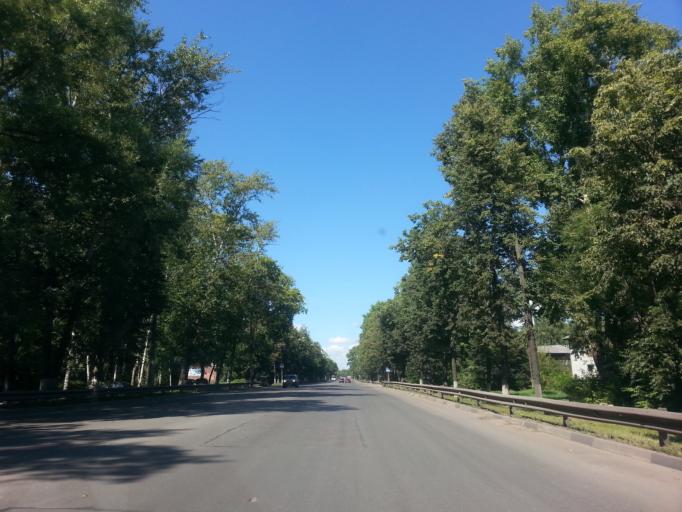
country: RU
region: Nizjnij Novgorod
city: Gorbatovka
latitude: 56.3407
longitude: 43.8437
